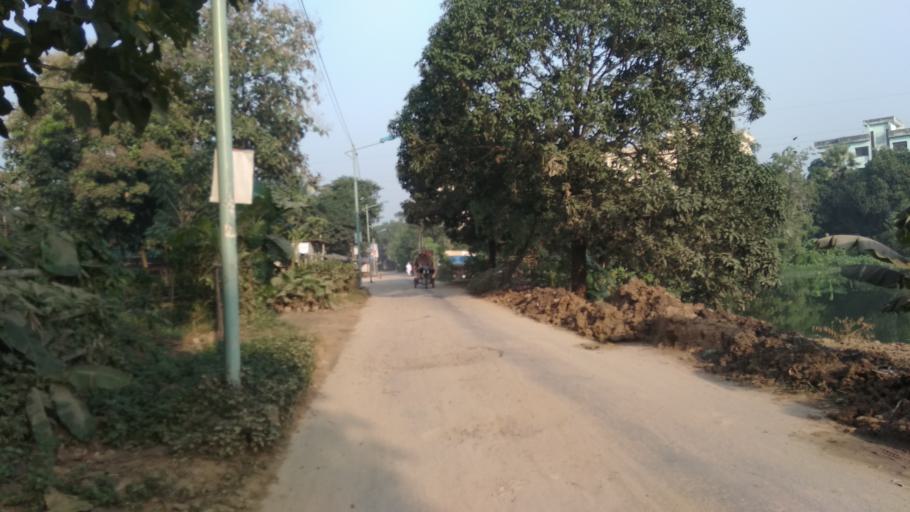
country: BD
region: Dhaka
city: Tungi
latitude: 23.8433
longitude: 90.4182
